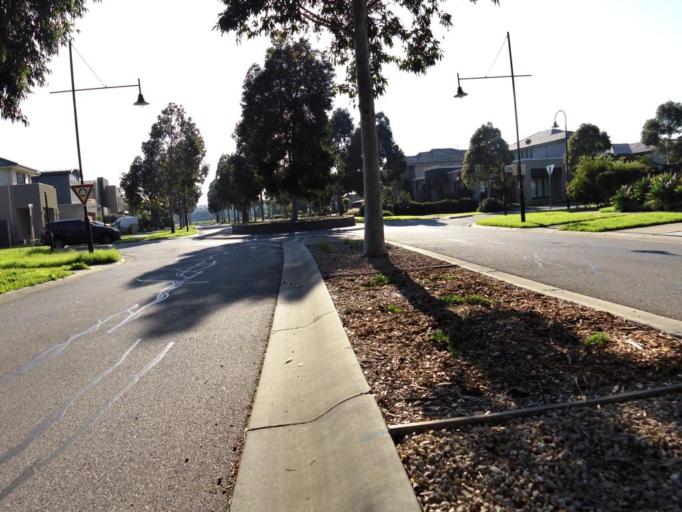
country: AU
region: Victoria
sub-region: Kingston
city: Waterways
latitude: -38.0124
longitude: 145.1319
